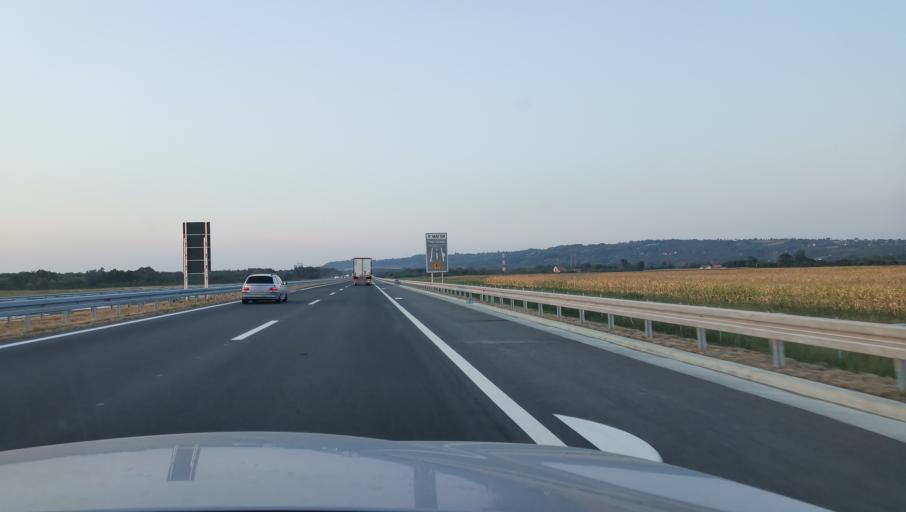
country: RS
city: Stubline
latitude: 44.5825
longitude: 20.1950
